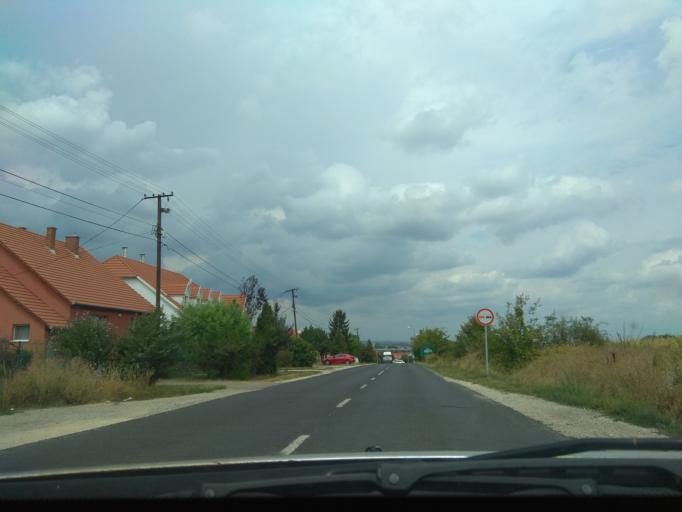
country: HU
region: Borsod-Abauj-Zemplen
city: Malyi
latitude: 48.0502
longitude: 20.7956
